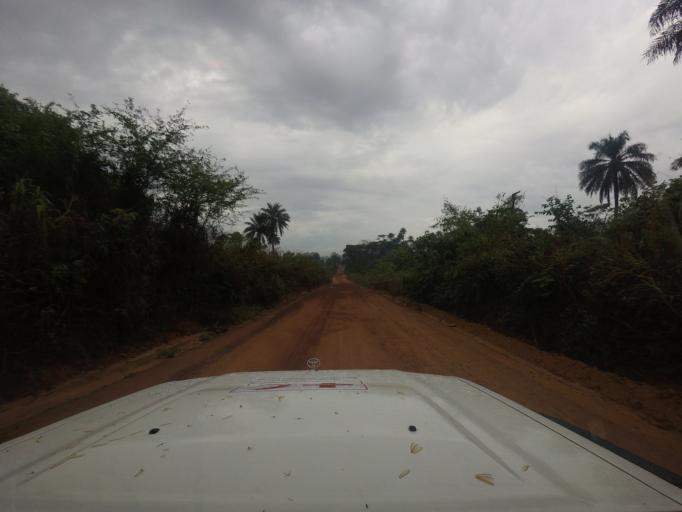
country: LR
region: Lofa
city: Voinjama
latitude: 8.4009
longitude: -9.7849
